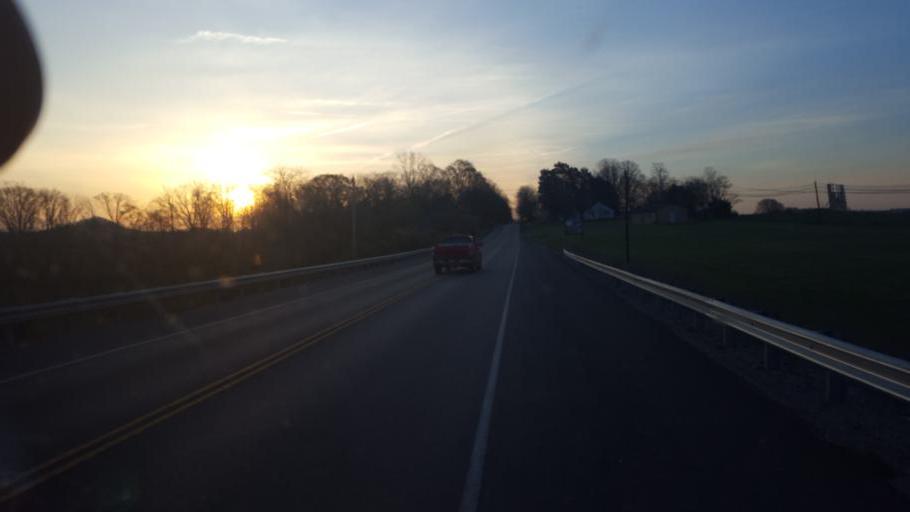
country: US
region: Kentucky
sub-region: Hart County
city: Munfordville
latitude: 37.2747
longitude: -85.9125
